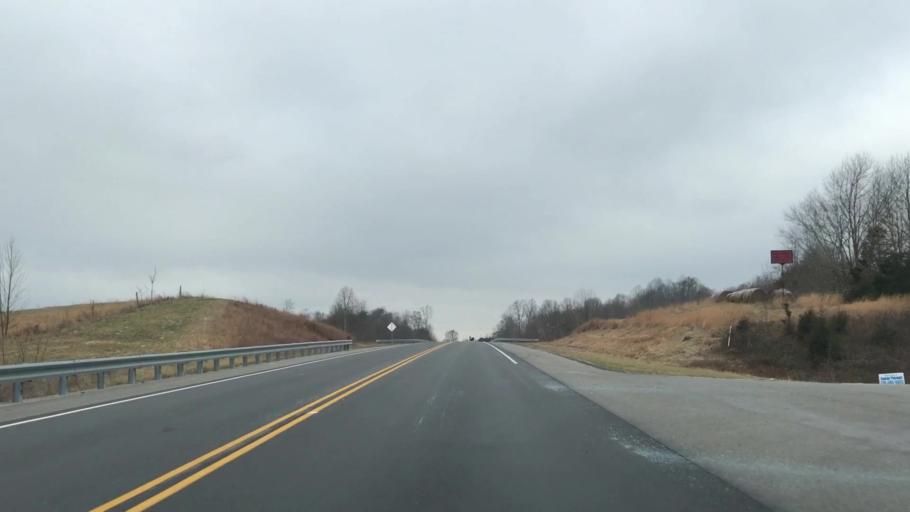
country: US
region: Kentucky
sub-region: Adair County
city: Columbia
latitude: 36.9698
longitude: -85.4283
